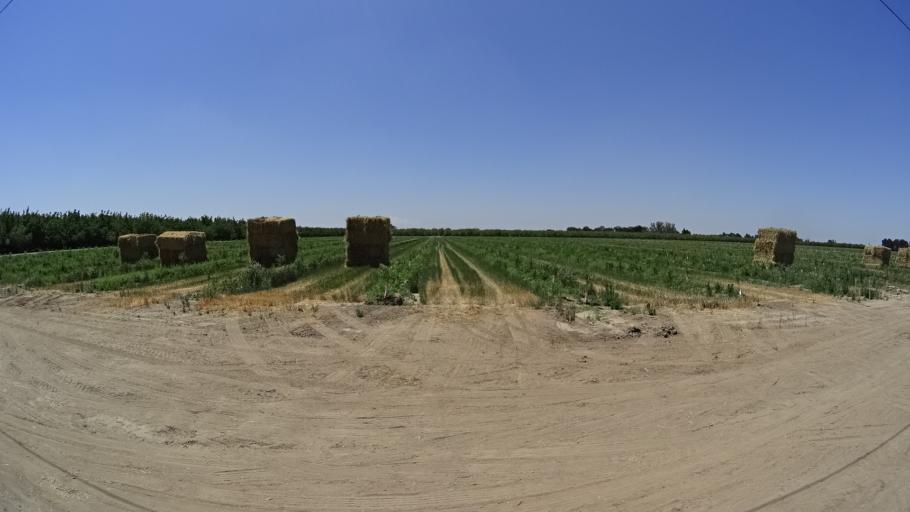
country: US
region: California
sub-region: Kings County
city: Lucerne
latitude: 36.4166
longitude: -119.6190
